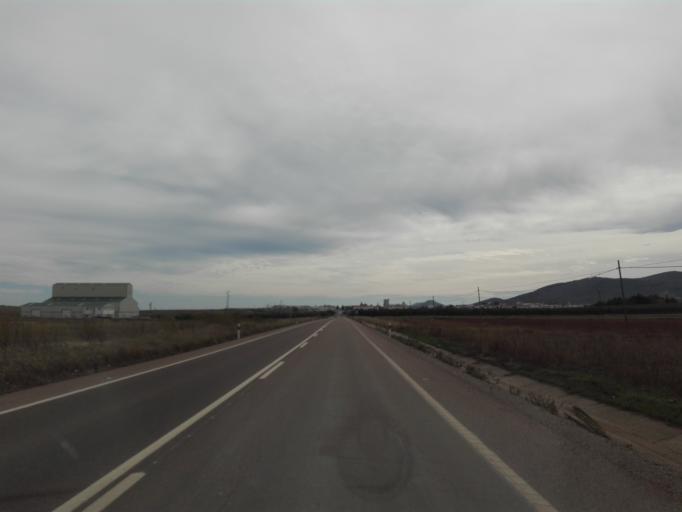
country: ES
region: Extremadura
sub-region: Provincia de Badajoz
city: Llerena
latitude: 38.2527
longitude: -6.0274
